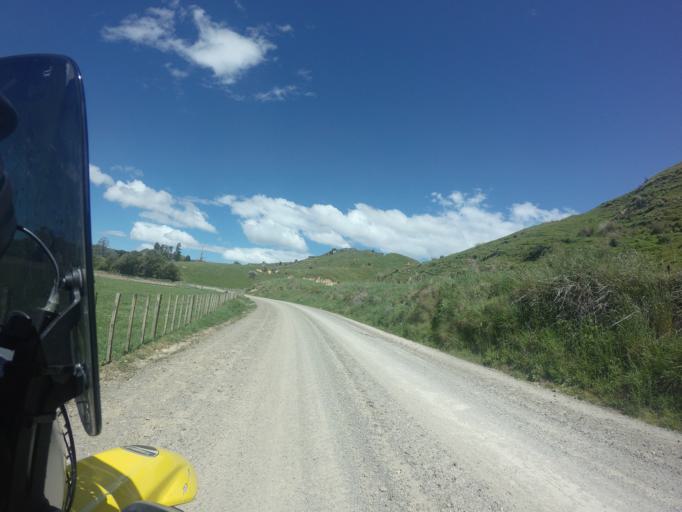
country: NZ
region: Hawke's Bay
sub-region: Wairoa District
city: Wairoa
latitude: -38.9873
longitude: 177.7010
